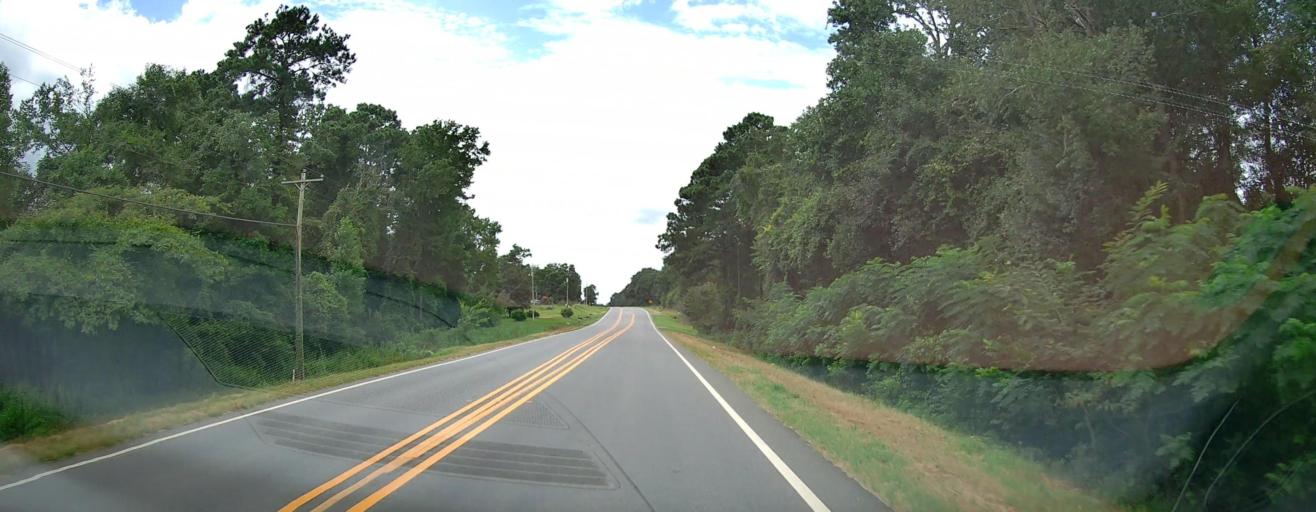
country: US
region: Georgia
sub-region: Macon County
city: Montezuma
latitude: 32.2927
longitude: -83.9429
